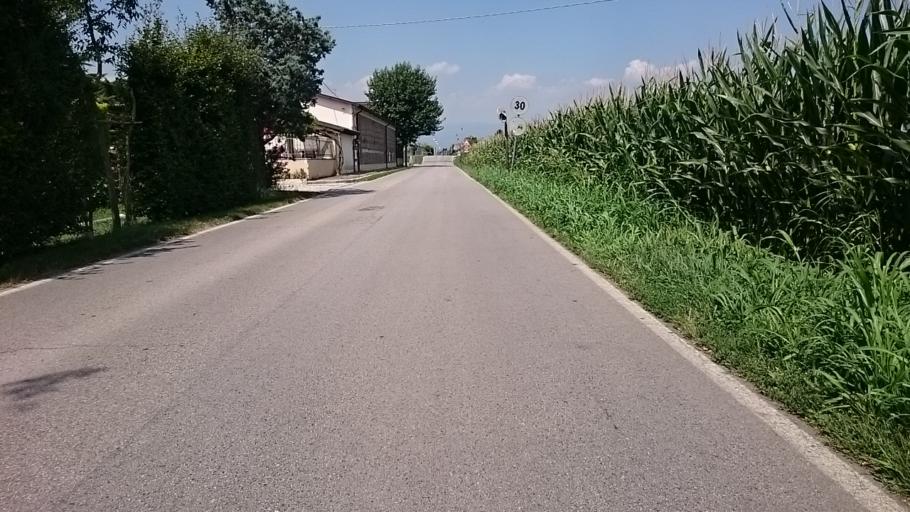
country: IT
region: Veneto
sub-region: Provincia di Padova
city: Fontaniva
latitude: 45.6521
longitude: 11.7590
